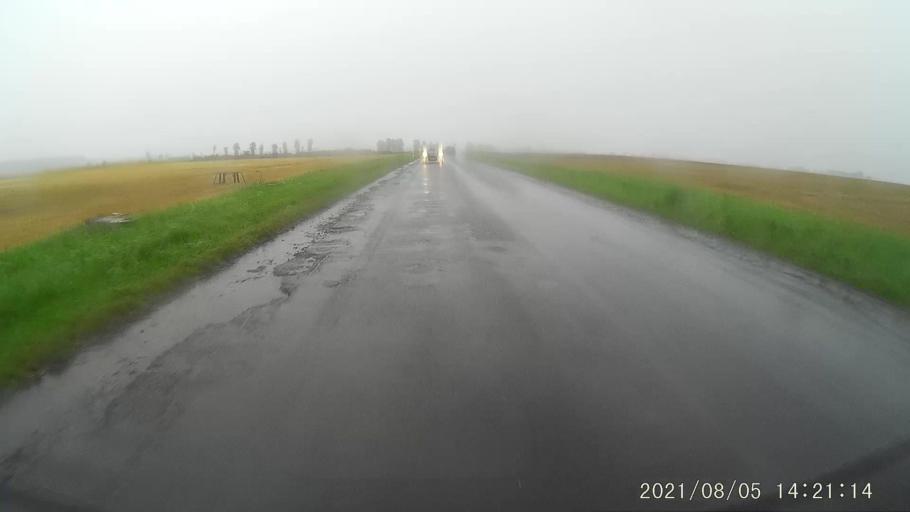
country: PL
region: Opole Voivodeship
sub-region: Powiat nyski
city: Korfantow
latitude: 50.4707
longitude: 17.6762
